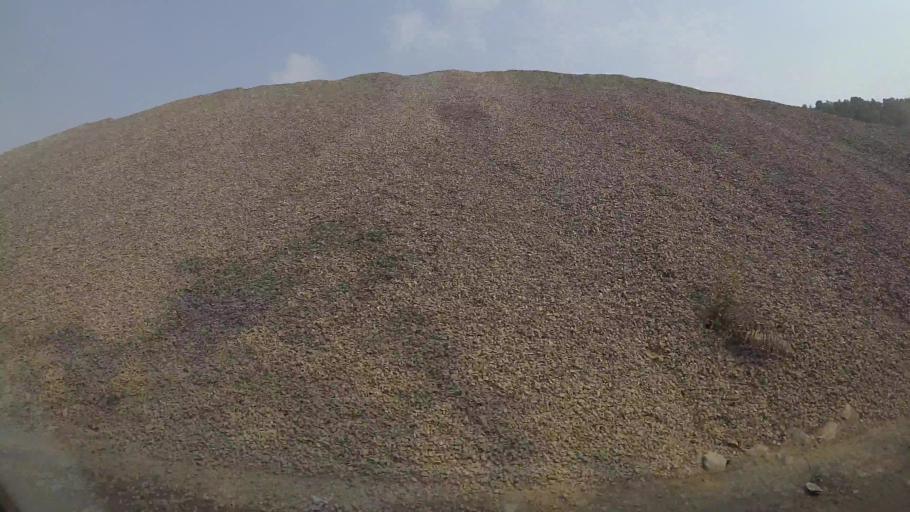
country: VN
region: Da Nang
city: Lien Chieu
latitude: 16.0404
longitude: 108.1594
